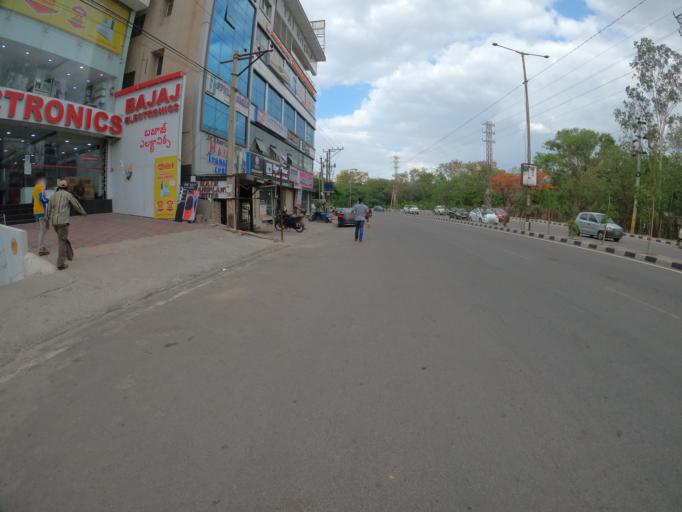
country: IN
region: Telangana
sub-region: Hyderabad
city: Hyderabad
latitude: 17.3616
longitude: 78.3927
